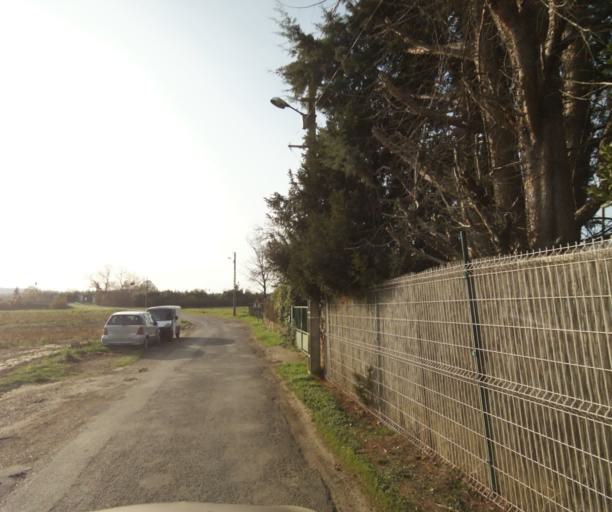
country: FR
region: Ile-de-France
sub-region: Departement des Yvelines
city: Chanteloup-les-Vignes
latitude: 48.9688
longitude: 2.0253
